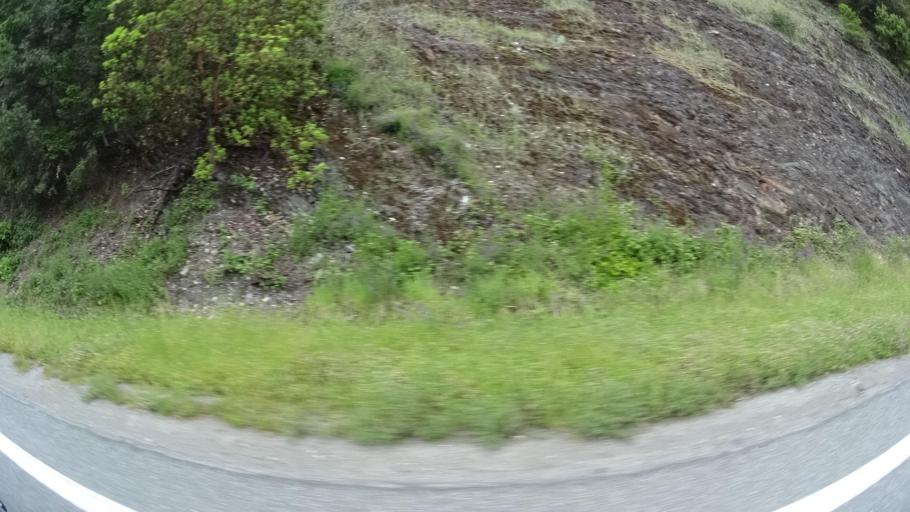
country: US
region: California
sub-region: Humboldt County
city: Willow Creek
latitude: 41.2813
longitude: -123.5842
